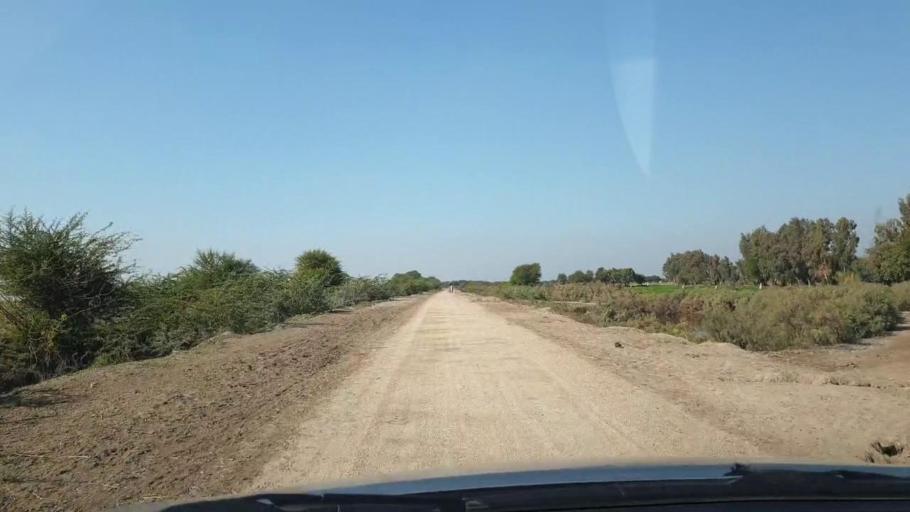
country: PK
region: Sindh
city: Jhol
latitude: 25.9226
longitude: 68.9588
